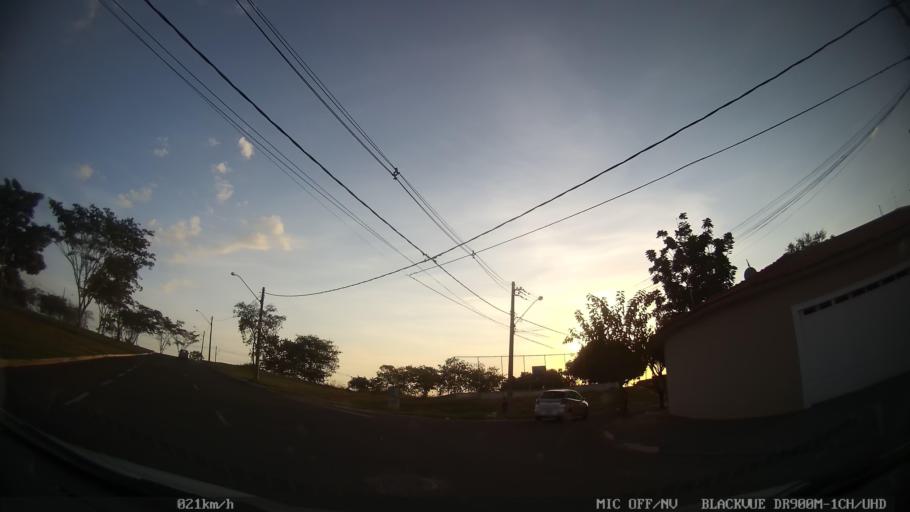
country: BR
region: Sao Paulo
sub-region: Ribeirao Preto
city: Ribeirao Preto
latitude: -21.1416
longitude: -47.8558
